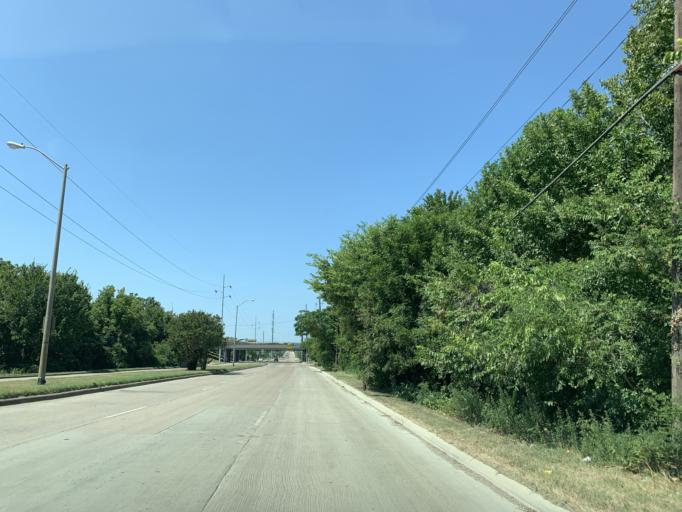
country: US
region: Texas
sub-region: Dallas County
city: Hutchins
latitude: 32.6828
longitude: -96.7424
